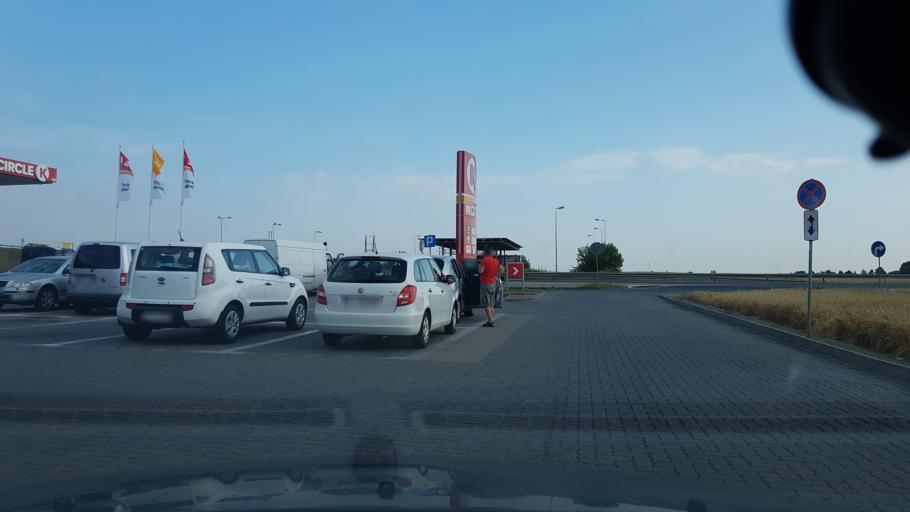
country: PL
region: Masovian Voivodeship
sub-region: Powiat nowodworski
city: Zakroczym
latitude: 52.4457
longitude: 20.6109
